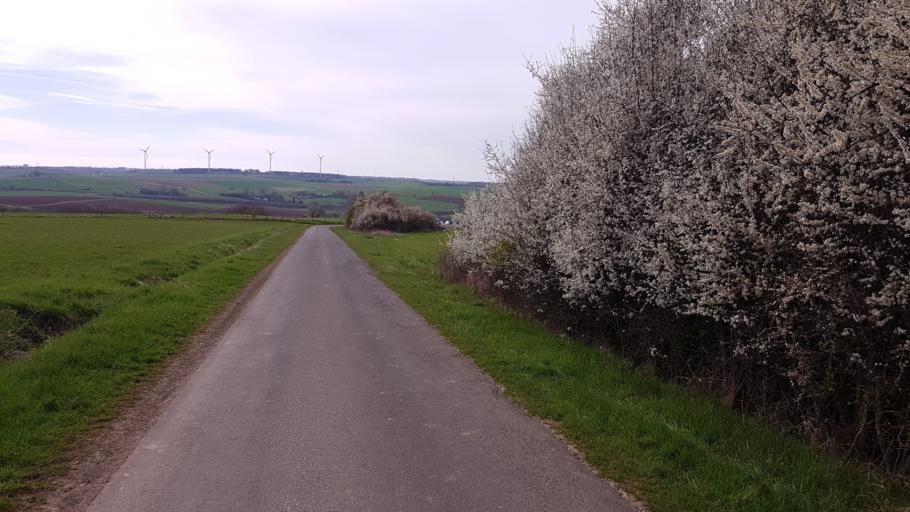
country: DE
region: Hesse
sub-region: Regierungsbezirk Giessen
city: Homberg
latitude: 50.6773
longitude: 9.0498
